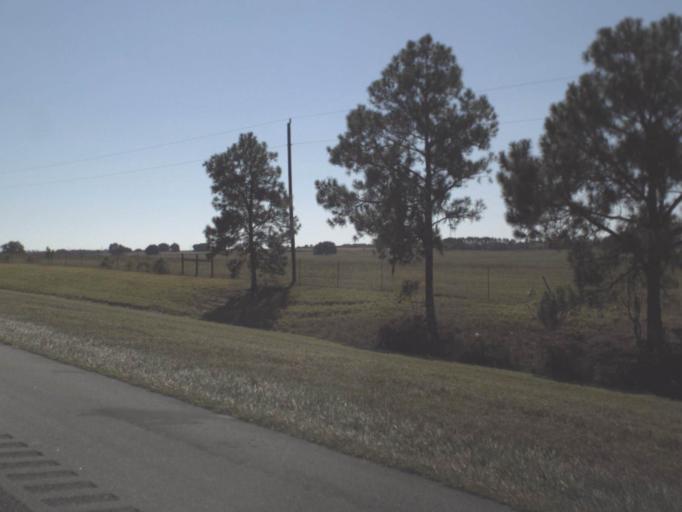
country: US
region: Florida
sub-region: Lake County
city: Hawthorne
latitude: 28.7659
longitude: -81.9500
